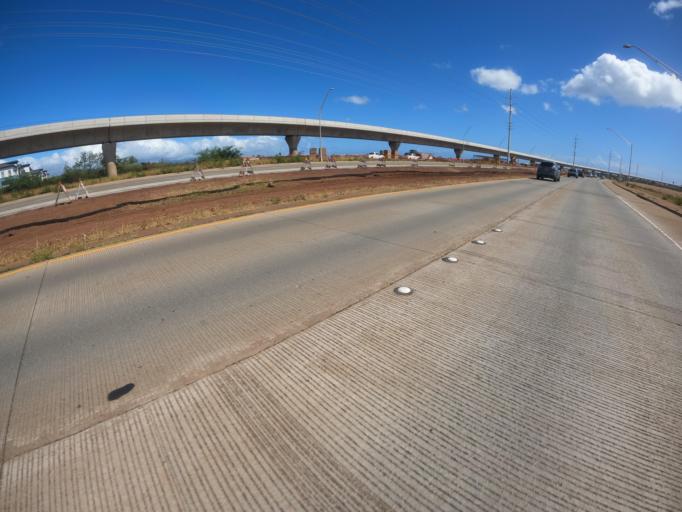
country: US
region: Hawaii
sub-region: Honolulu County
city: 'Ewa Villages
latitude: 21.3555
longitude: -158.0501
